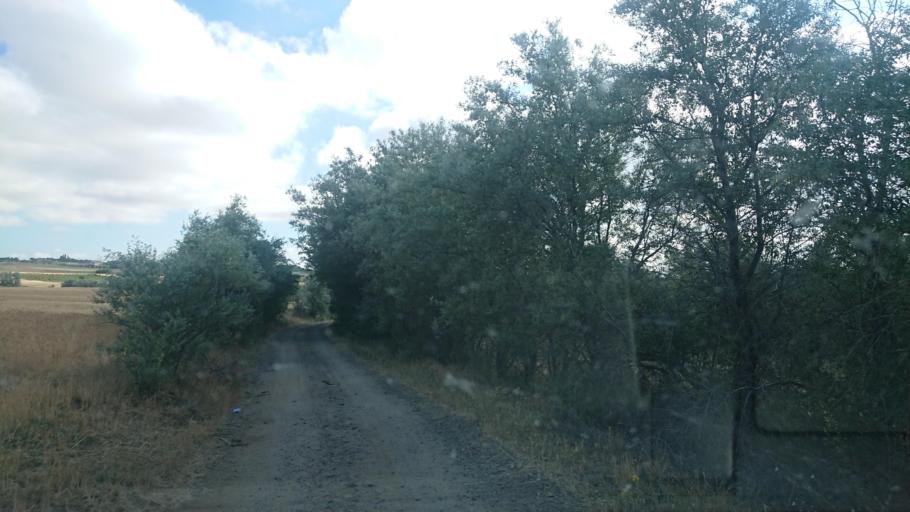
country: TR
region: Aksaray
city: Agacoren
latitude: 38.8600
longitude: 33.9393
